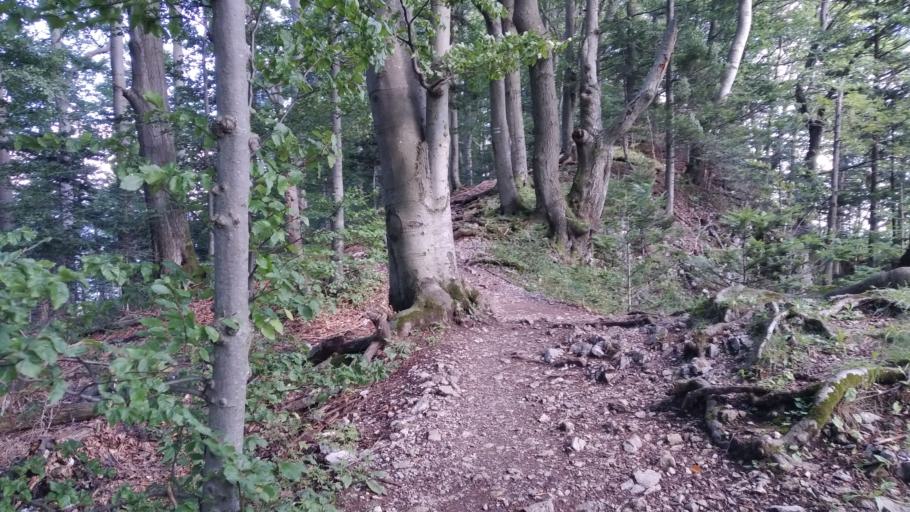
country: PL
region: Lesser Poland Voivodeship
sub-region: Powiat nowotarski
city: Kroscienko nad Dunajcem
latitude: 49.4223
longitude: 20.4347
